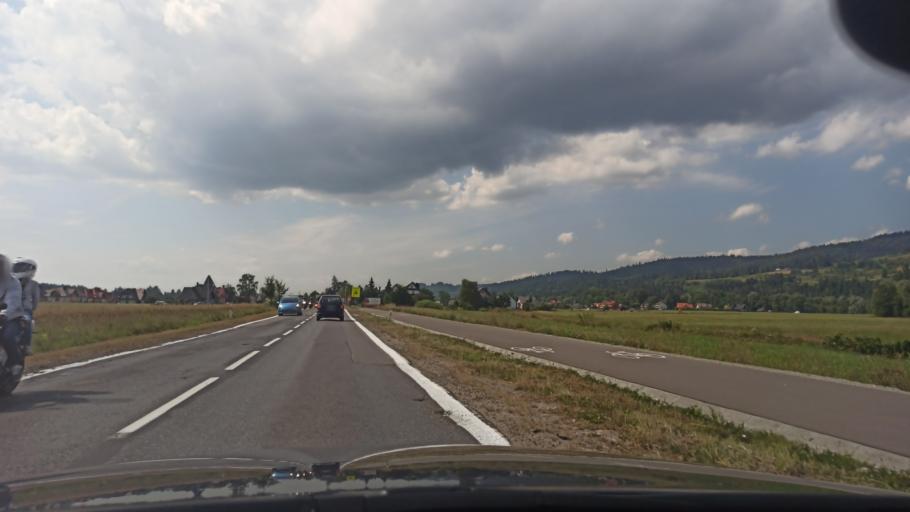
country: PL
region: Lesser Poland Voivodeship
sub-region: Powiat nowotarski
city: Lopuszna
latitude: 49.4728
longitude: 20.1818
